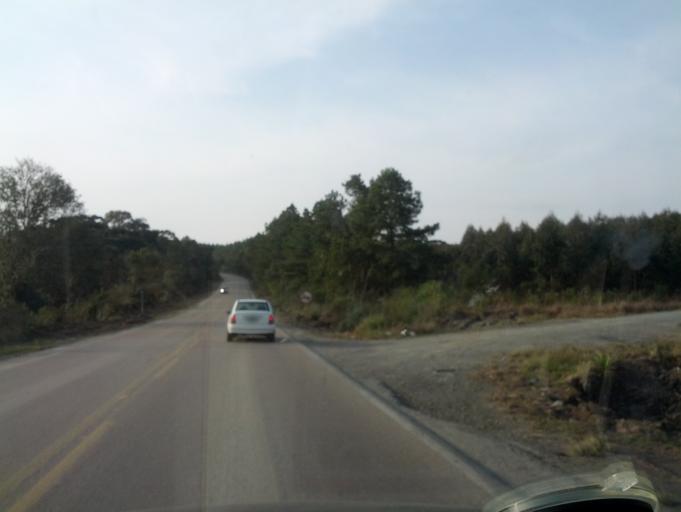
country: BR
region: Santa Catarina
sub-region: Otacilio Costa
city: Otacilio Costa
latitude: -27.4581
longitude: -50.1228
